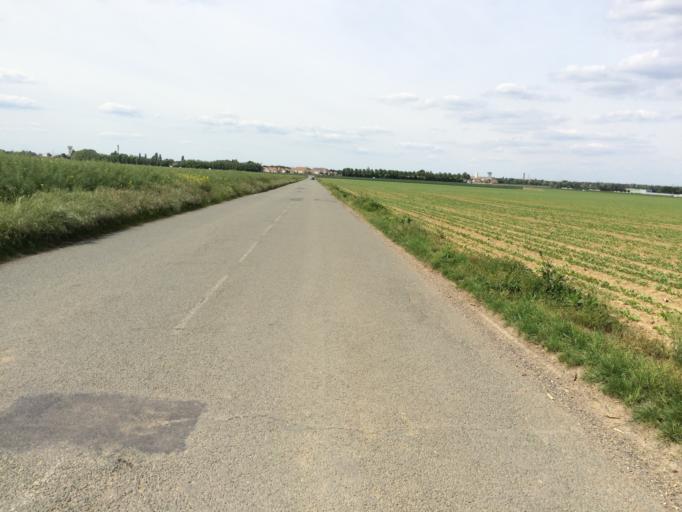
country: FR
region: Ile-de-France
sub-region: Departement de l'Essonne
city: Saclay
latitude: 48.7215
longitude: 2.1812
